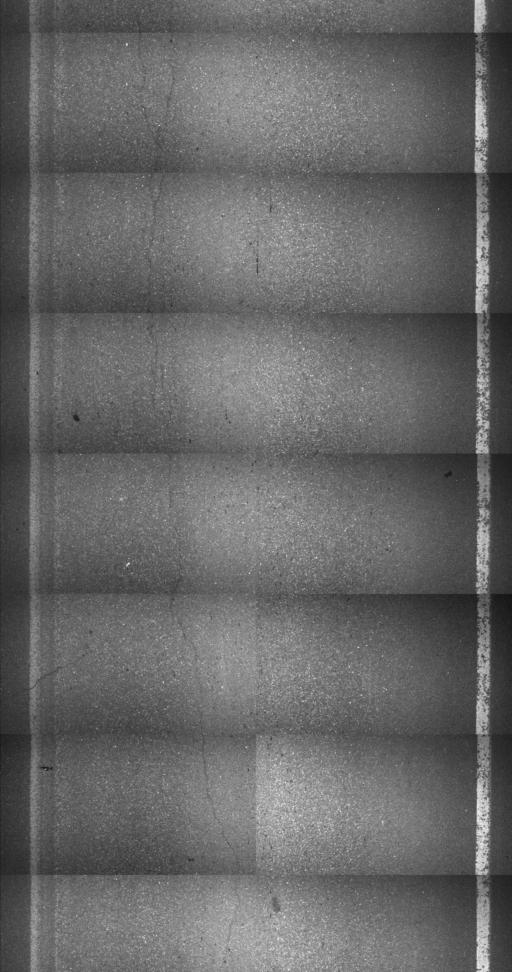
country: US
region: Vermont
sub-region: Orleans County
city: Newport
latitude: 44.9145
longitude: -72.2381
